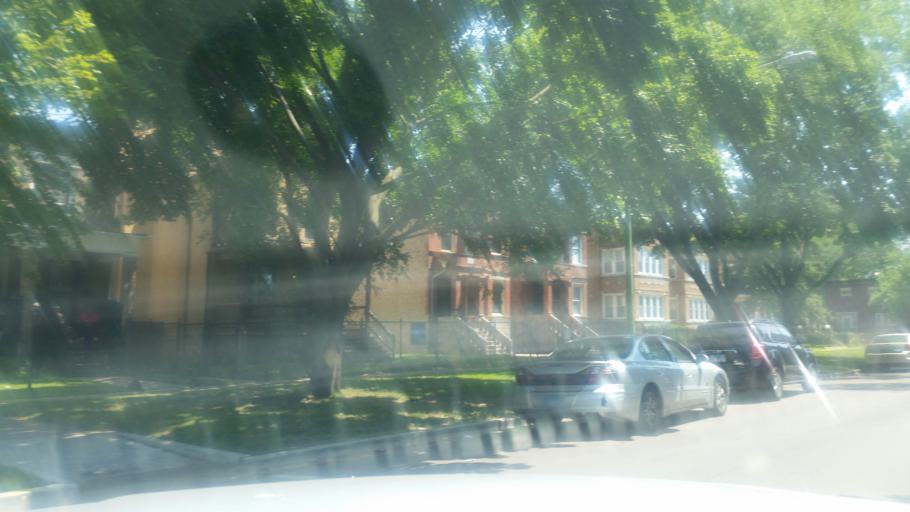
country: US
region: Illinois
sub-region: Cook County
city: Chicago
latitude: 41.7684
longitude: -87.6170
